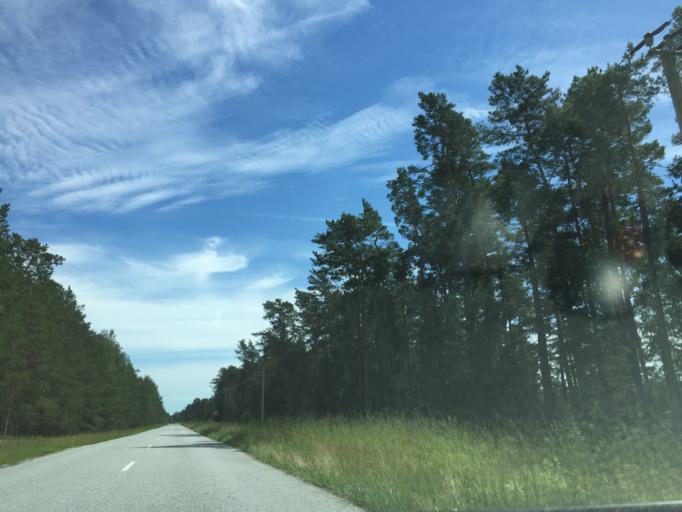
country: LV
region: Talsu Rajons
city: Valdemarpils
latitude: 57.5860
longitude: 22.6161
